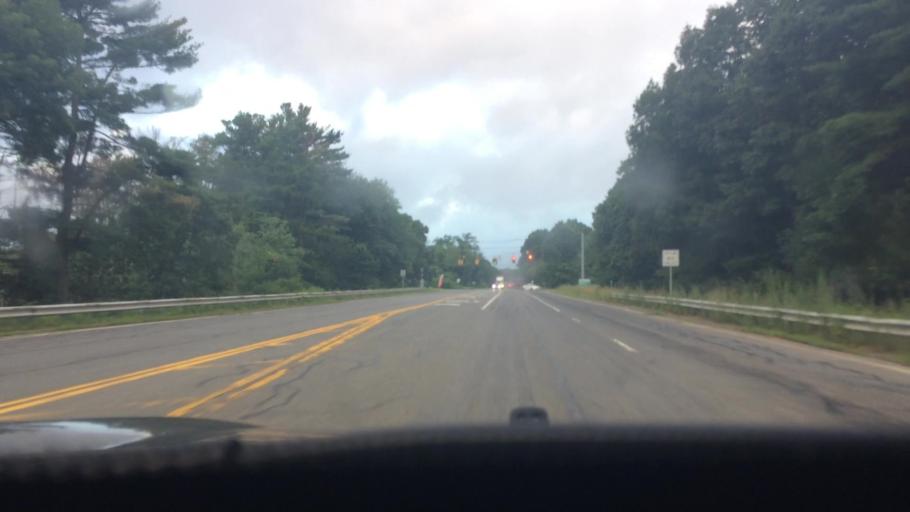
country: US
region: Massachusetts
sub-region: Middlesex County
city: Wilmington
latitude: 42.5927
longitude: -71.1458
